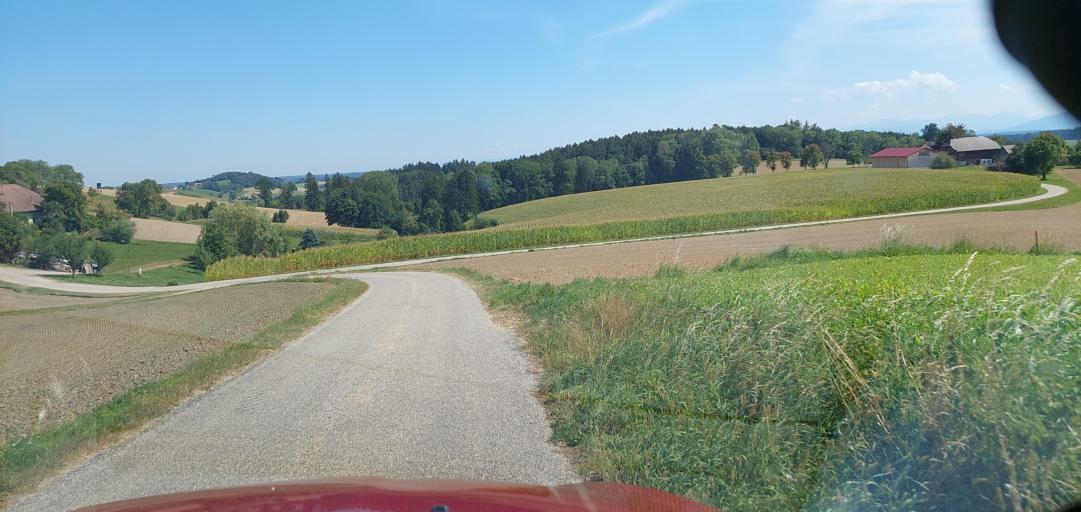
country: AT
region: Upper Austria
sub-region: Wels-Land
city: Pennewang
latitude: 48.1412
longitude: 13.8466
